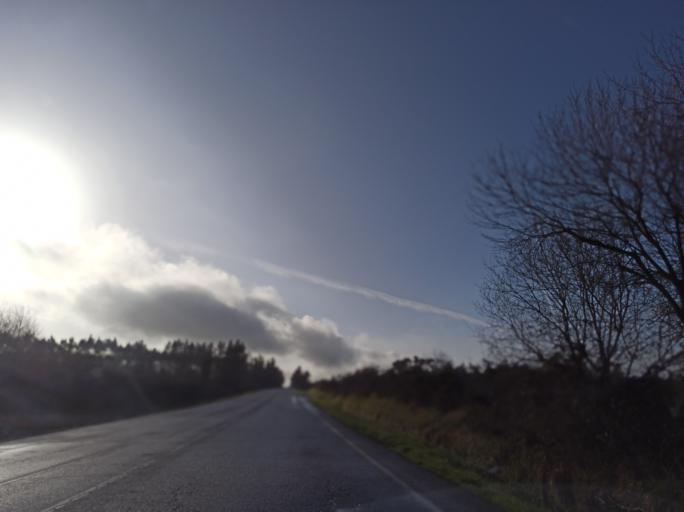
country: ES
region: Galicia
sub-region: Provincia da Coruna
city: Curtis
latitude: 43.1124
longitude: -8.0258
